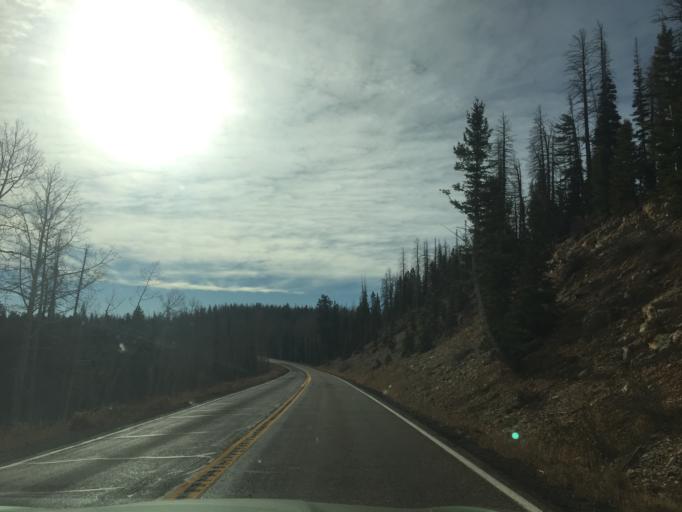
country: US
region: Utah
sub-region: Iron County
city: Parowan
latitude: 37.5366
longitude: -112.7739
